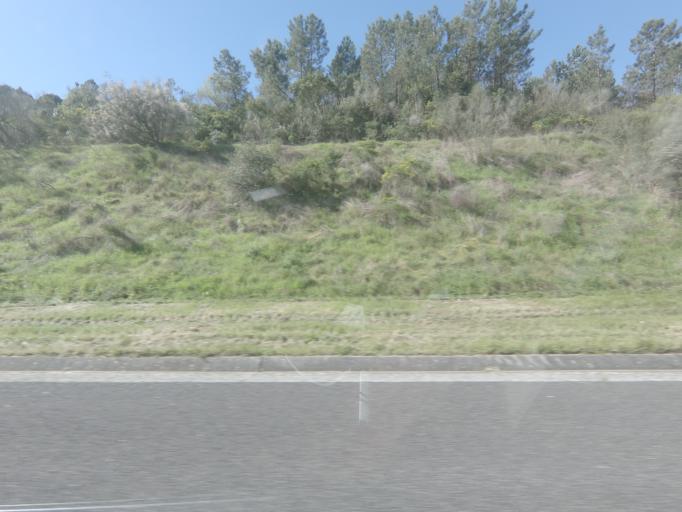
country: PT
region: Leiria
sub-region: Leiria
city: Caranguejeira
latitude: 39.7278
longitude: -8.7181
